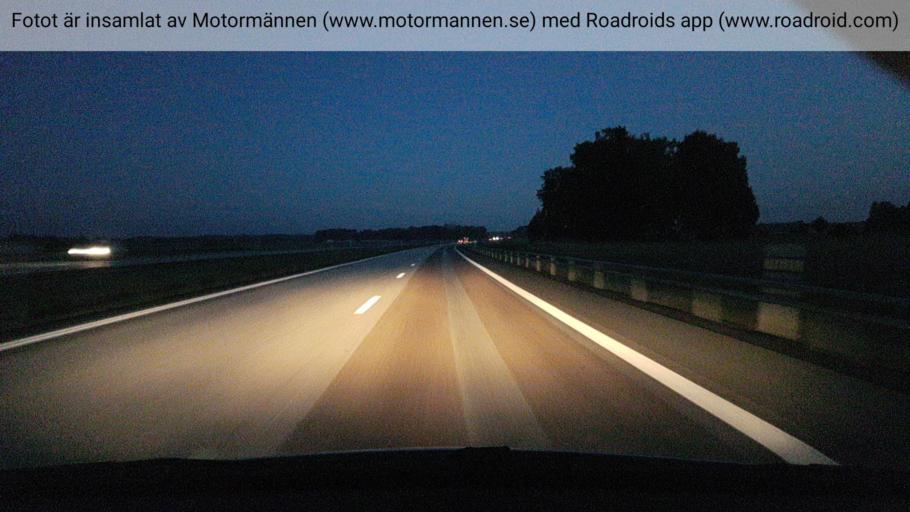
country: SE
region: Uppsala
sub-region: Osthammars Kommun
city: Bjorklinge
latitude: 60.0749
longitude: 17.6048
